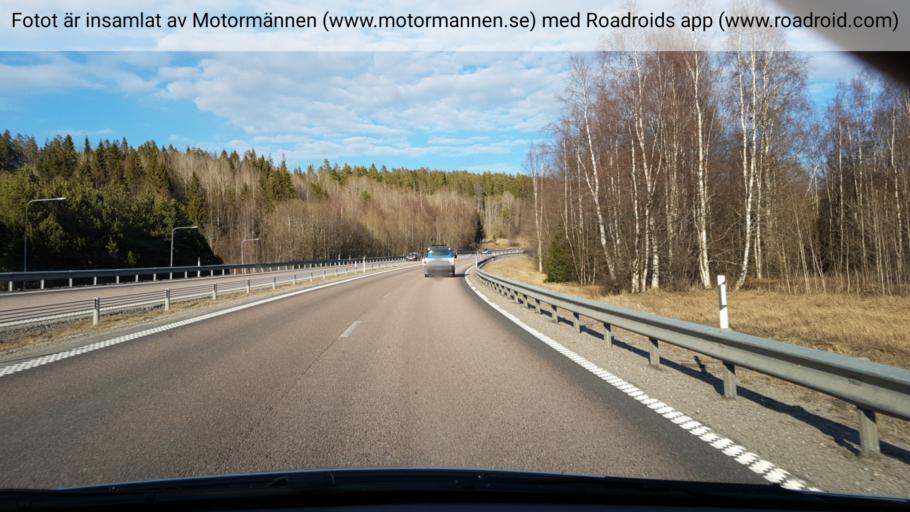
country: SE
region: Vaesternorrland
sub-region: OErnskoeldsviks Kommun
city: Ornskoldsvik
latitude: 63.3166
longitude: 18.7971
